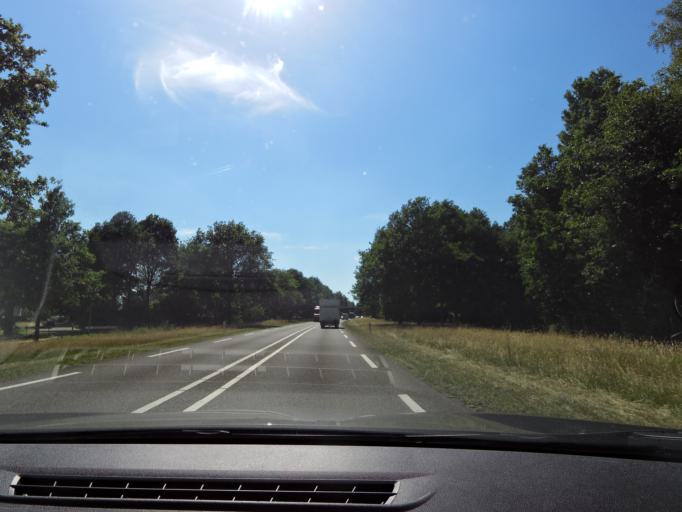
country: NL
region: Gelderland
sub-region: Oost Gelre
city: Lichtenvoorde
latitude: 52.0002
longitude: 6.5855
